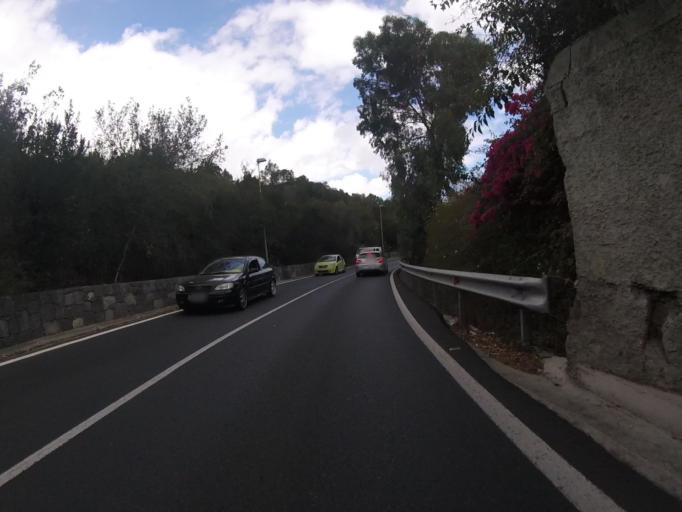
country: ES
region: Canary Islands
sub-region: Provincia de Las Palmas
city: Santa Brigida
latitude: 28.0231
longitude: -15.5137
